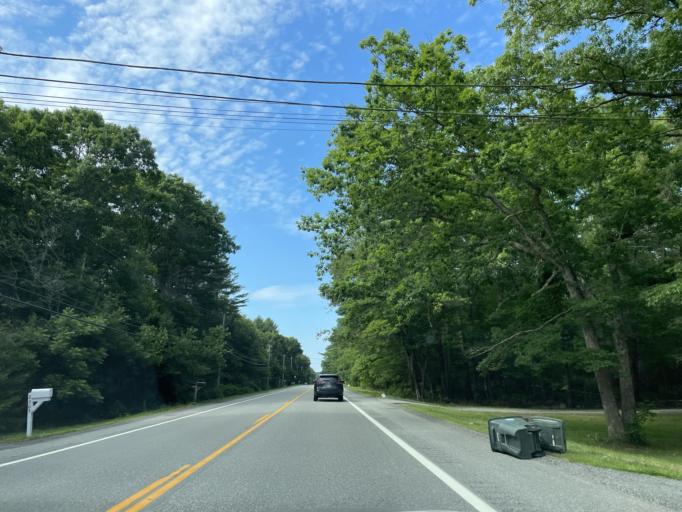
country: US
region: Rhode Island
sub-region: Kent County
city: Coventry
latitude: 41.6626
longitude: -71.6950
